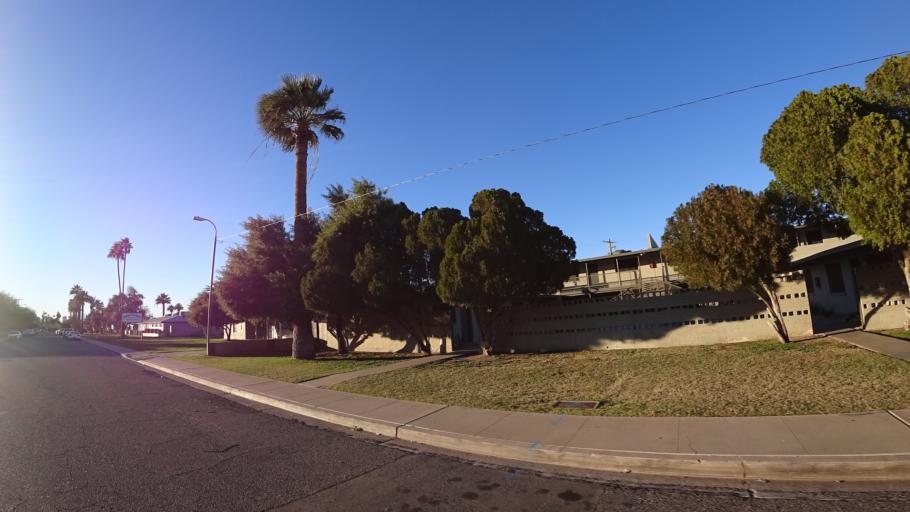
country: US
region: Arizona
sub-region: Maricopa County
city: Phoenix
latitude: 33.4822
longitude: -112.0310
